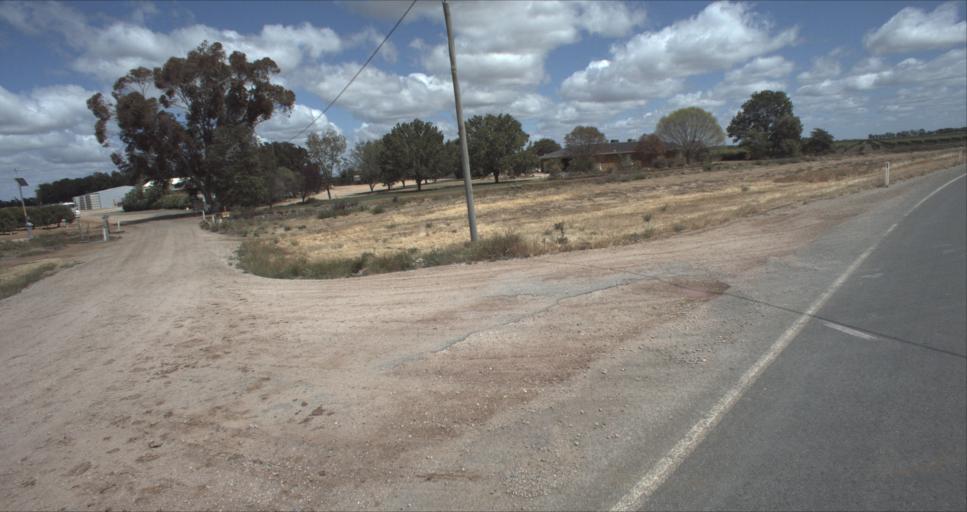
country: AU
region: New South Wales
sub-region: Murrumbidgee Shire
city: Darlington Point
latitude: -34.4943
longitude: 146.1684
